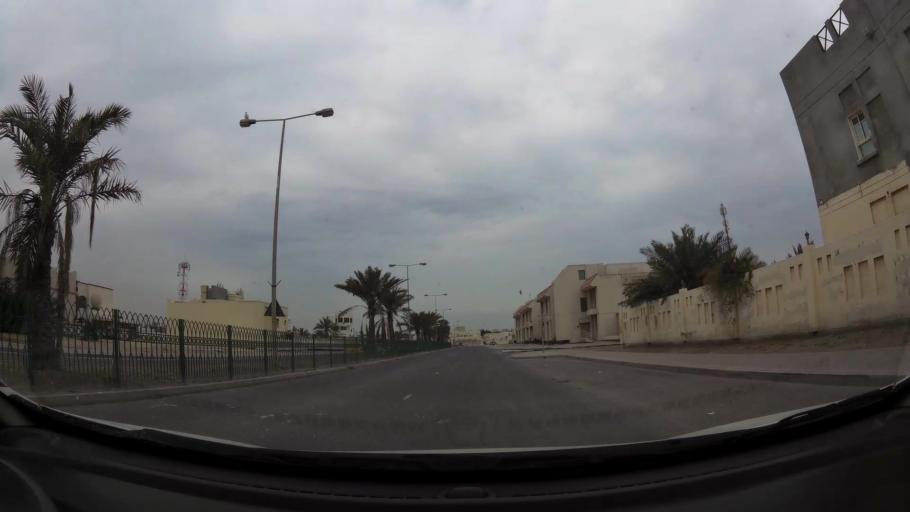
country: BH
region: Northern
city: Sitrah
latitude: 26.1588
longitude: 50.6187
